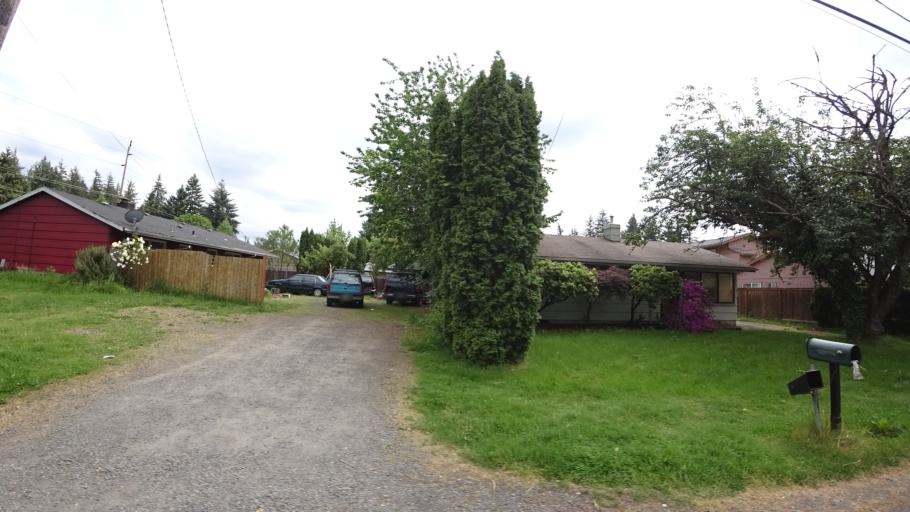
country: US
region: Oregon
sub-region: Multnomah County
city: Gresham
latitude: 45.5136
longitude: -122.4763
